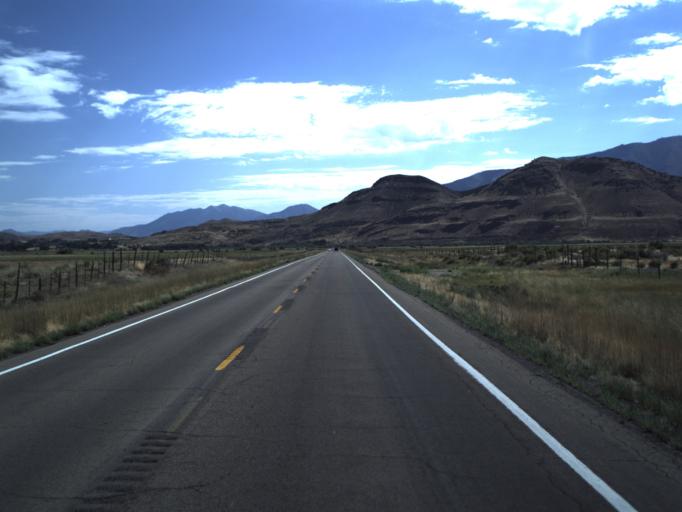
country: US
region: Utah
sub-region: Utah County
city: Genola
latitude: 39.9549
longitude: -111.8871
